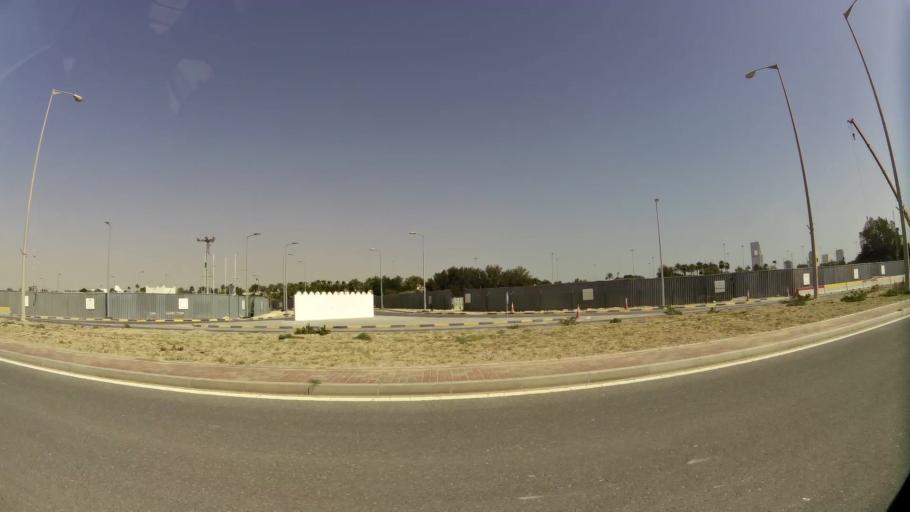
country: QA
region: Baladiyat ad Dawhah
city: Doha
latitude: 25.3772
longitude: 51.5057
